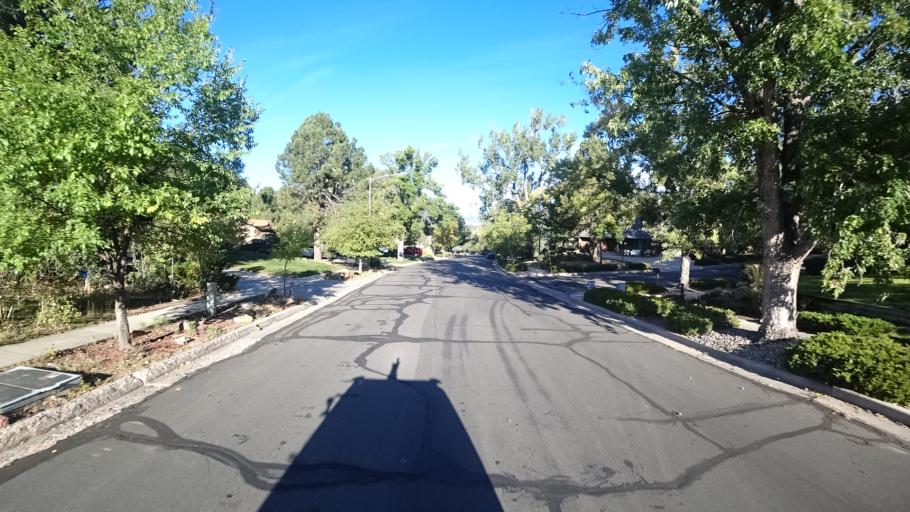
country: US
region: Colorado
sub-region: El Paso County
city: Cimarron Hills
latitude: 38.8867
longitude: -104.7679
